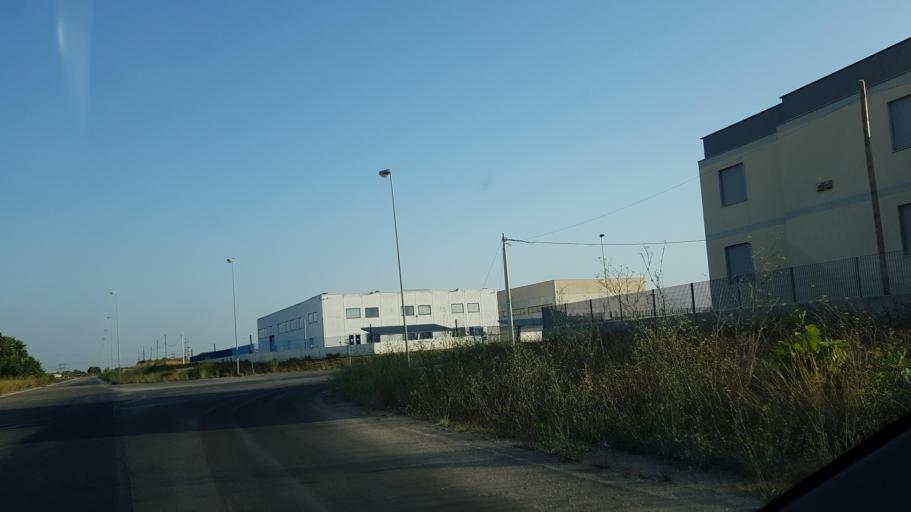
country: IT
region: Apulia
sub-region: Provincia di Brindisi
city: La Rosa
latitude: 40.6281
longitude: 17.9762
